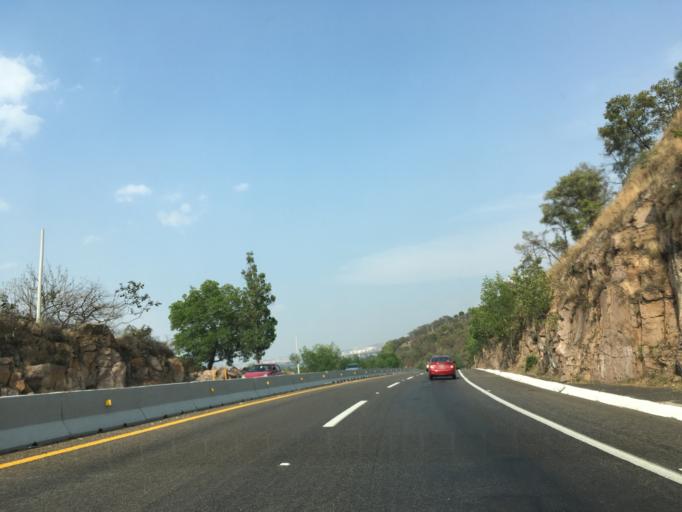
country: MX
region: Michoacan
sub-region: Morelia
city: La Mintzita (Piedra Dura)
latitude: 19.6380
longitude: -101.2692
